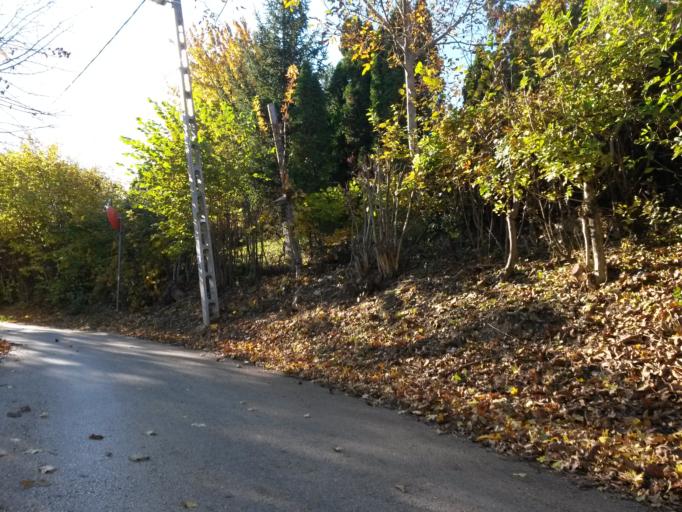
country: HU
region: Pest
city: Budaors
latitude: 47.4812
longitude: 18.9779
